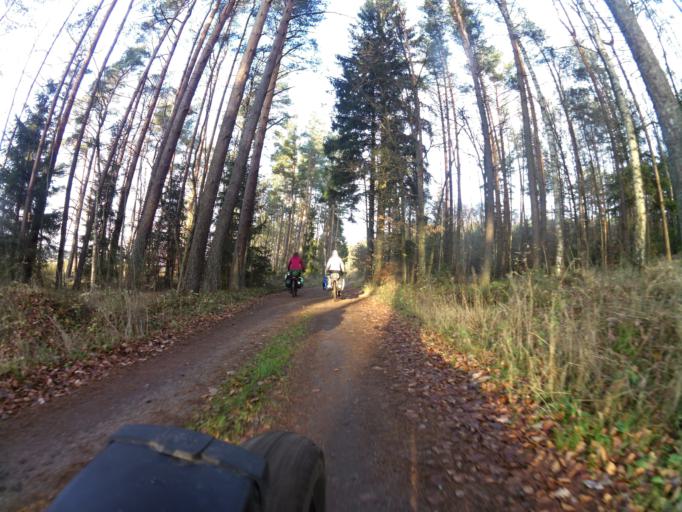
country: PL
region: West Pomeranian Voivodeship
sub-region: Powiat koszalinski
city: Polanow
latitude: 54.0955
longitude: 16.6481
